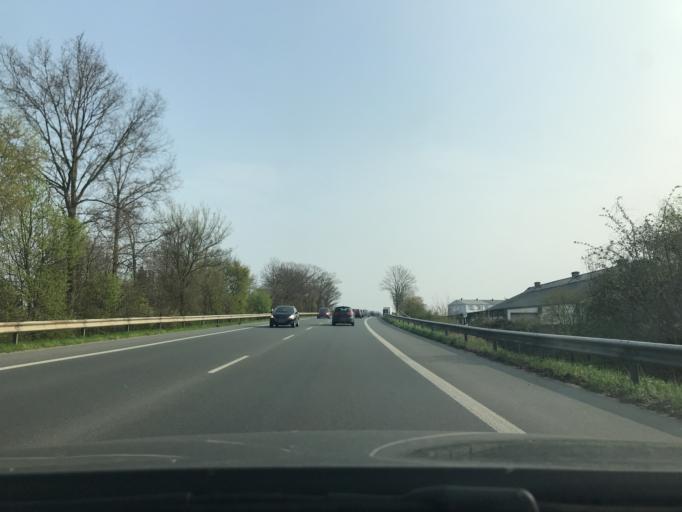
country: DE
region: North Rhine-Westphalia
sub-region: Regierungsbezirk Dusseldorf
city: Weeze
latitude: 51.6270
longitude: 6.2072
